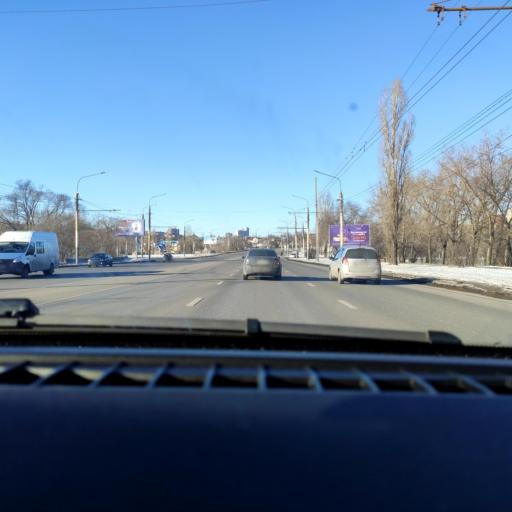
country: RU
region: Voronezj
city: Voronezh
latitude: 51.6357
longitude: 39.2126
